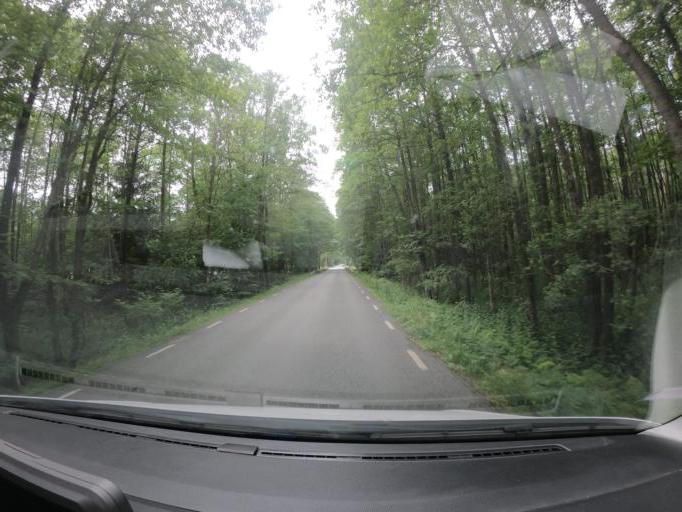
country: SE
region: Skane
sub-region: Hoors Kommun
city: Hoeoer
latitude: 56.0531
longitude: 13.5256
